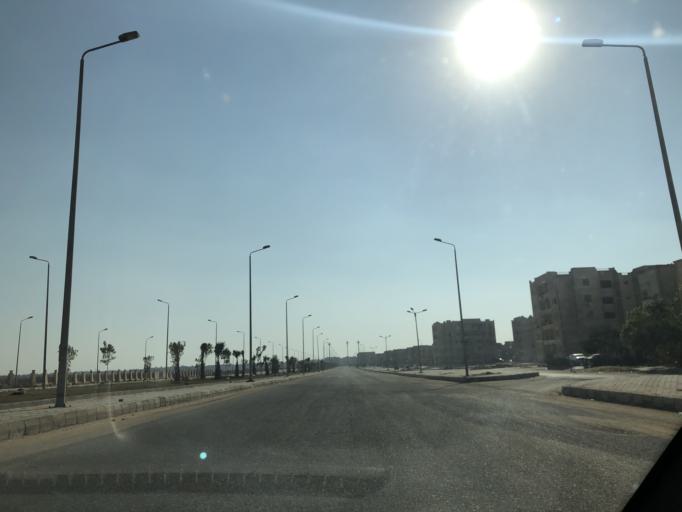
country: EG
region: Al Jizah
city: Madinat Sittah Uktubar
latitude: 29.9269
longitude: 31.0679
